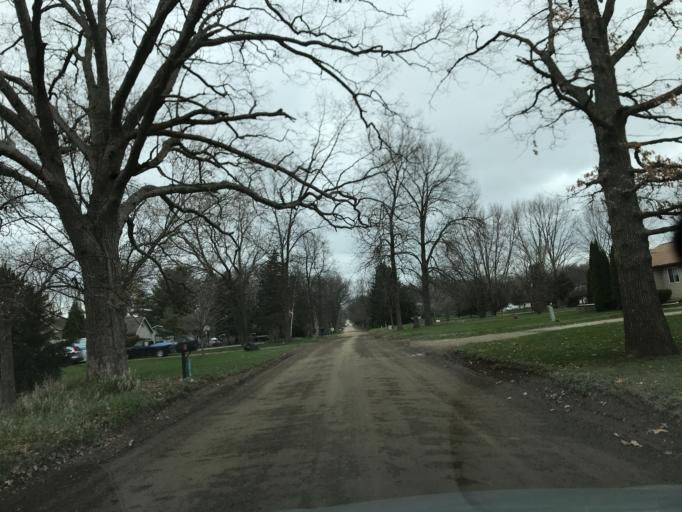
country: US
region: Michigan
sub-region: Oakland County
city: South Lyon
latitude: 42.4808
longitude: -83.6681
